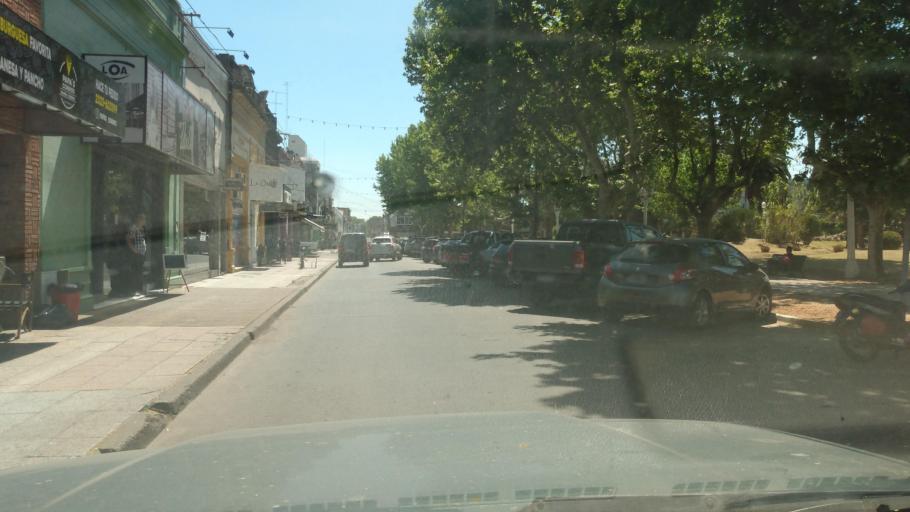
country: AR
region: Buenos Aires
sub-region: Partido de Lujan
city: Lujan
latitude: -34.5667
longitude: -59.1158
